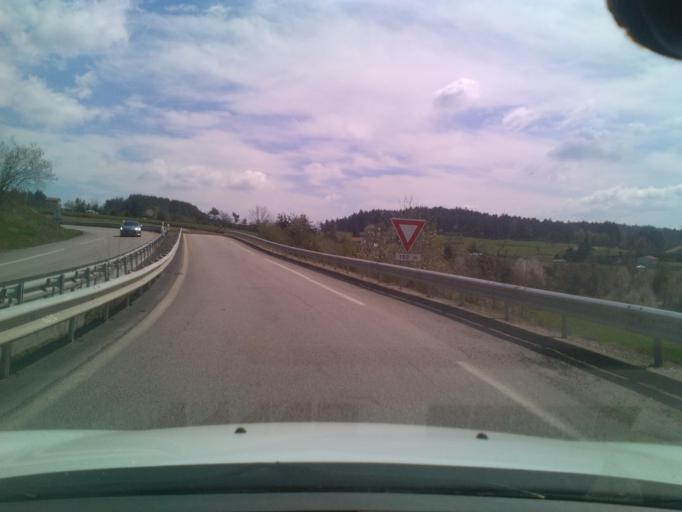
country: FR
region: Auvergne
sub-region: Departement de la Haute-Loire
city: La Seauve-sur-Semene
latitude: 45.3139
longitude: 4.2286
